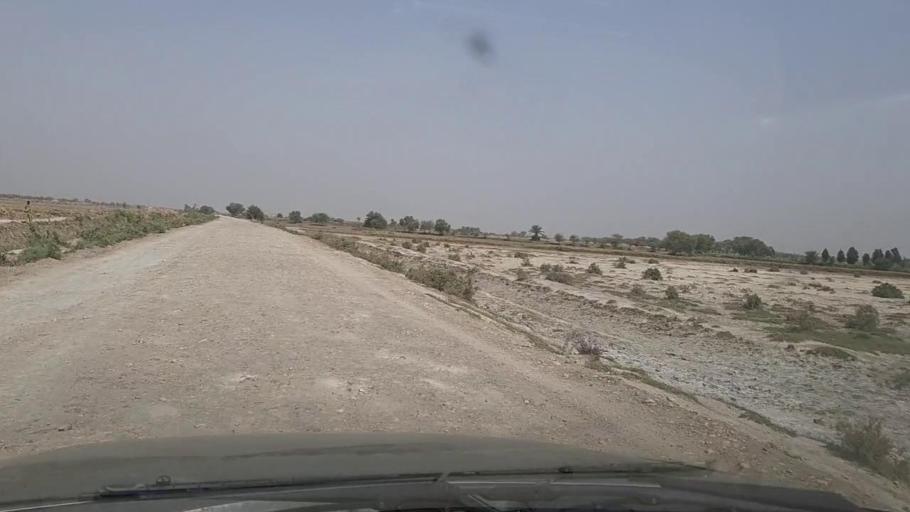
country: PK
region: Sindh
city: Thul
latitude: 28.4068
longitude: 68.7011
